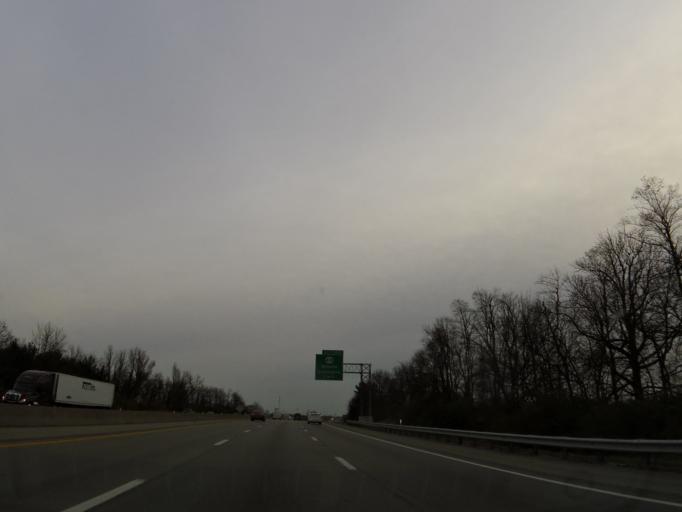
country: US
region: Kentucky
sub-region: Fayette County
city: Lexington
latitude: 37.9800
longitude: -84.3889
